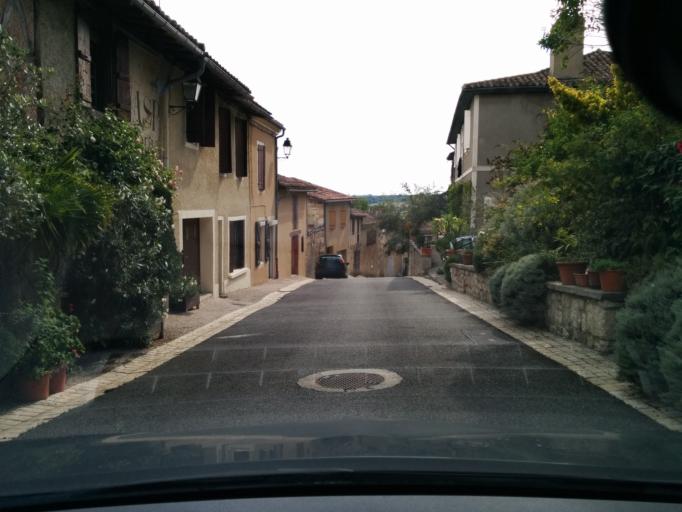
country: FR
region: Midi-Pyrenees
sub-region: Departement du Gers
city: Aubiet
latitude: 43.5754
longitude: 0.7244
